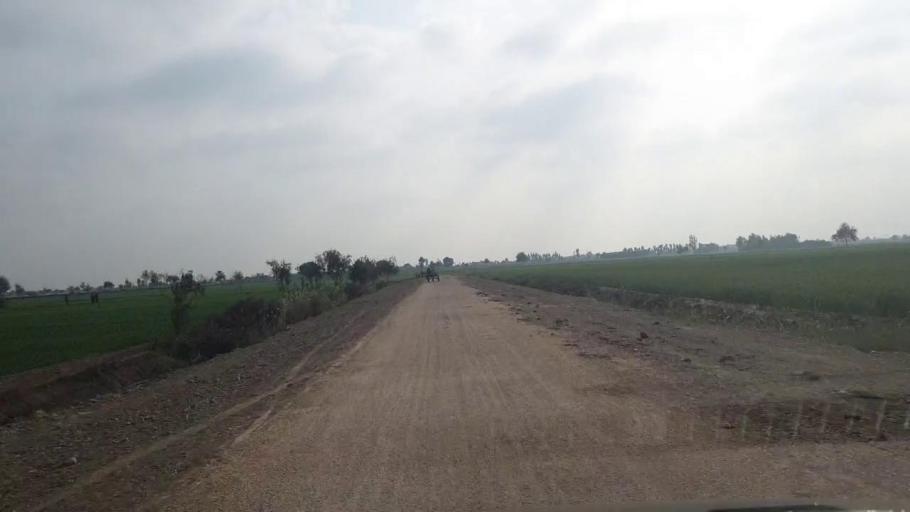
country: PK
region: Sindh
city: Shahdadpur
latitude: 25.8998
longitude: 68.6577
